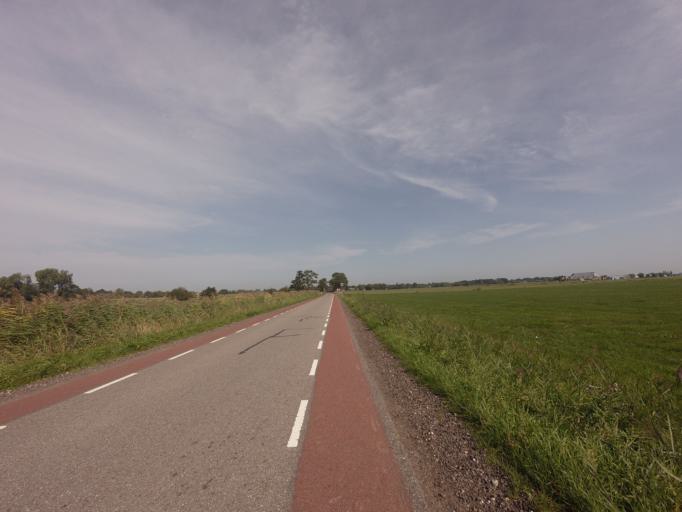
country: NL
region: Groningen
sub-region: Gemeente Leek
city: Leek
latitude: 53.2133
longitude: 6.3459
